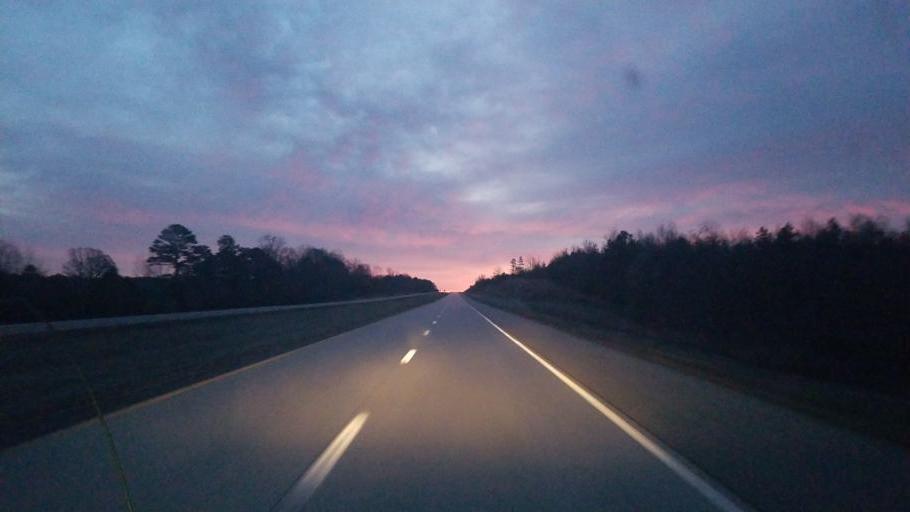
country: US
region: Missouri
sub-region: Shannon County
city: Winona
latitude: 36.9988
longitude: -91.4177
